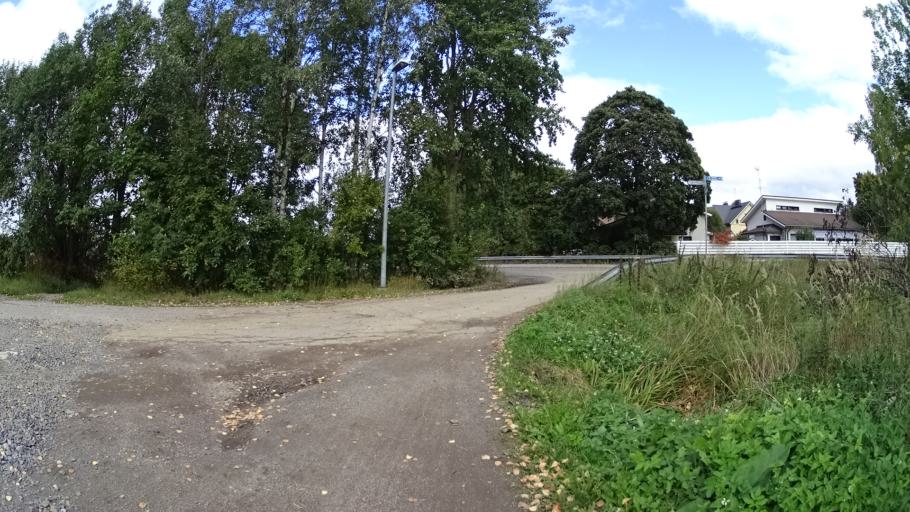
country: FI
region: Uusimaa
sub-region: Helsinki
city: Vantaa
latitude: 60.2500
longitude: 25.0285
